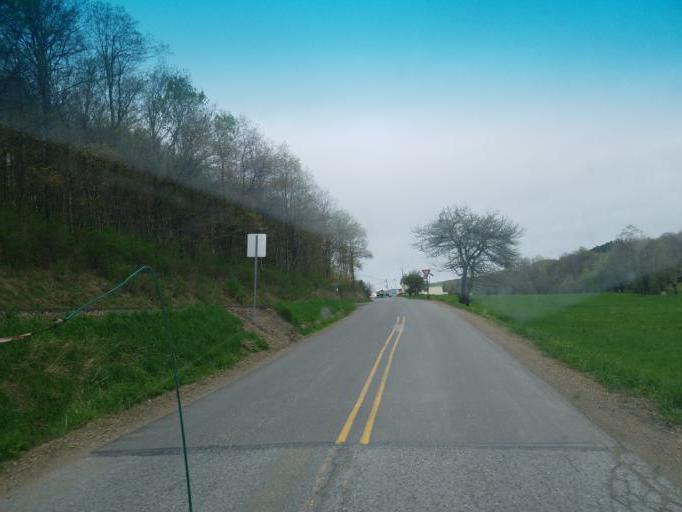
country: US
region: Pennsylvania
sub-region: Potter County
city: Galeton
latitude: 41.8950
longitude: -77.7593
